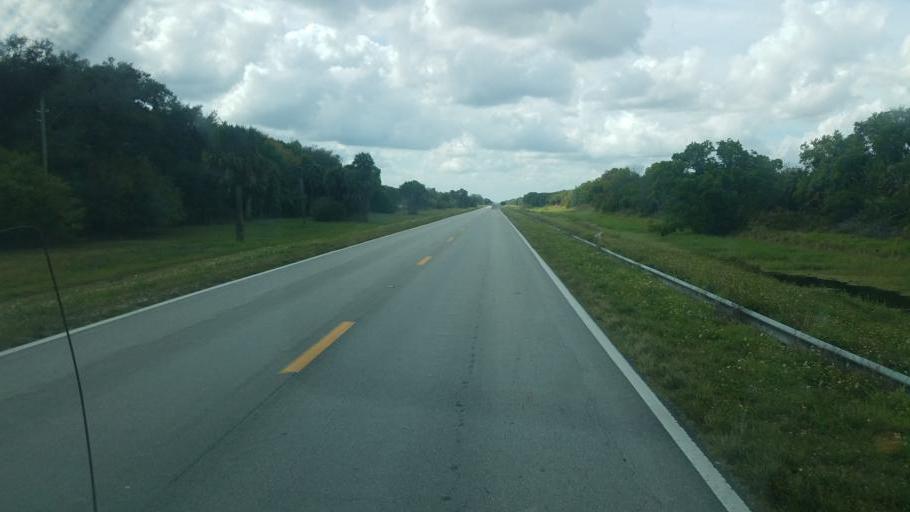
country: US
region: Florida
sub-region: Saint Lucie County
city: Lakewood Park
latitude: 27.4481
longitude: -80.5732
